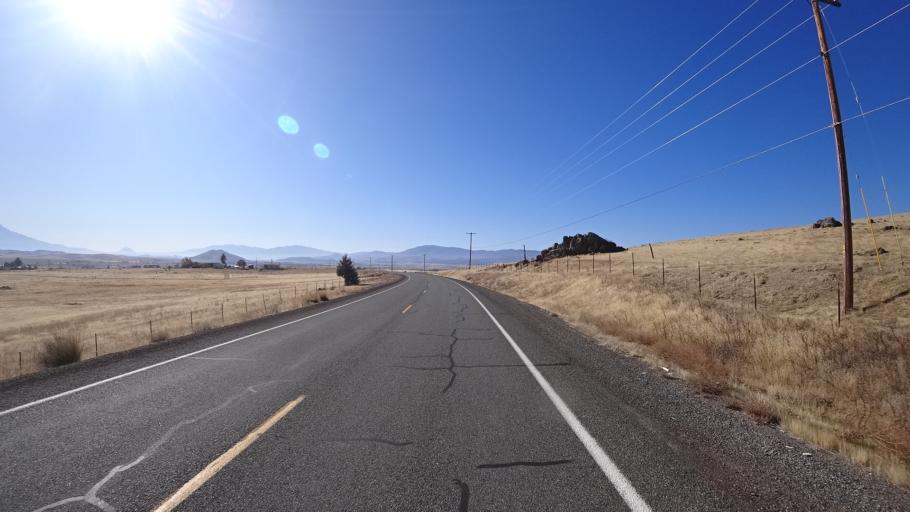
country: US
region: California
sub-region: Siskiyou County
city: Montague
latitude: 41.7768
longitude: -122.5237
